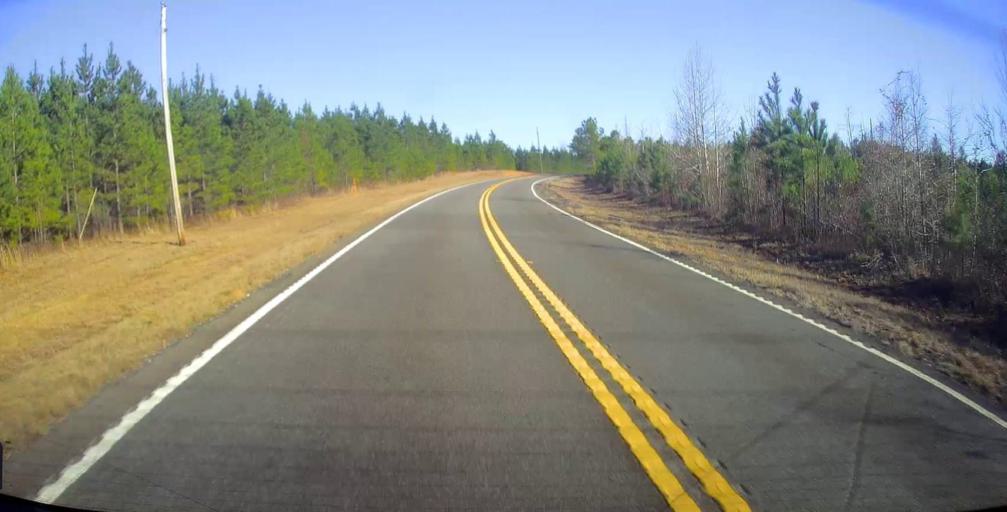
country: US
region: Georgia
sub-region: Talbot County
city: Talbotton
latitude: 32.6500
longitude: -84.3907
